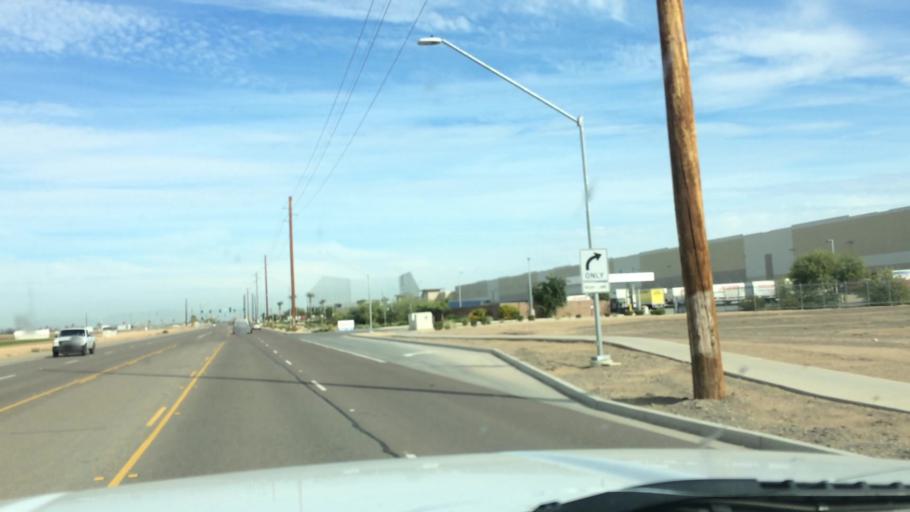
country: US
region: Arizona
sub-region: Maricopa County
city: Tolleson
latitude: 33.5160
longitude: -112.2724
